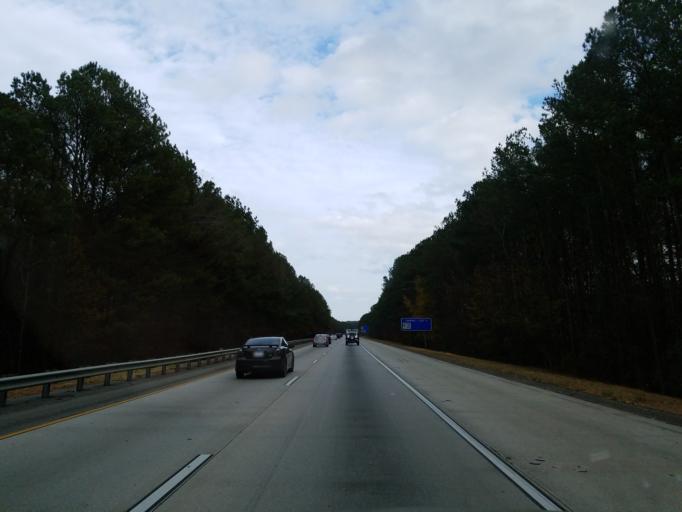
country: US
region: Georgia
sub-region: Carroll County
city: Mount Zion
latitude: 33.6882
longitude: -85.2174
